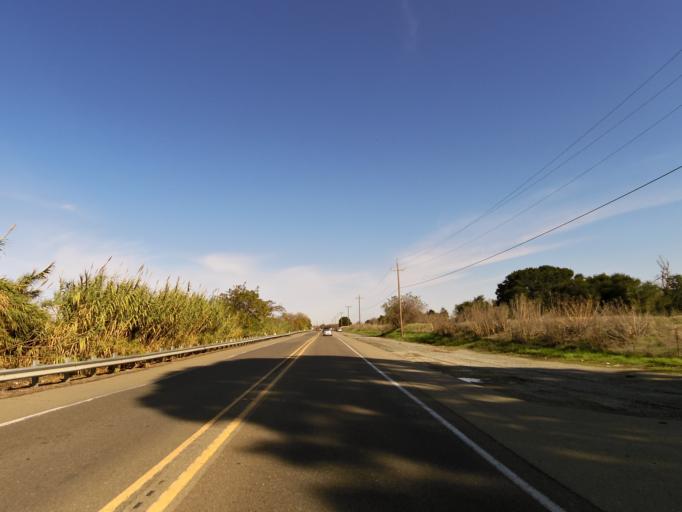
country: US
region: California
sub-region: Solano County
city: Rio Vista
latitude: 38.1145
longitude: -121.6964
